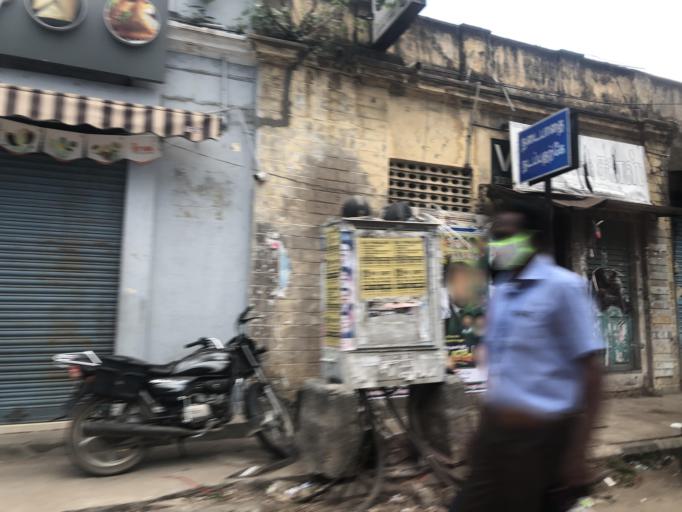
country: IN
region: Tamil Nadu
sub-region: Chennai
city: Chetput
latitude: 13.0631
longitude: 80.2670
